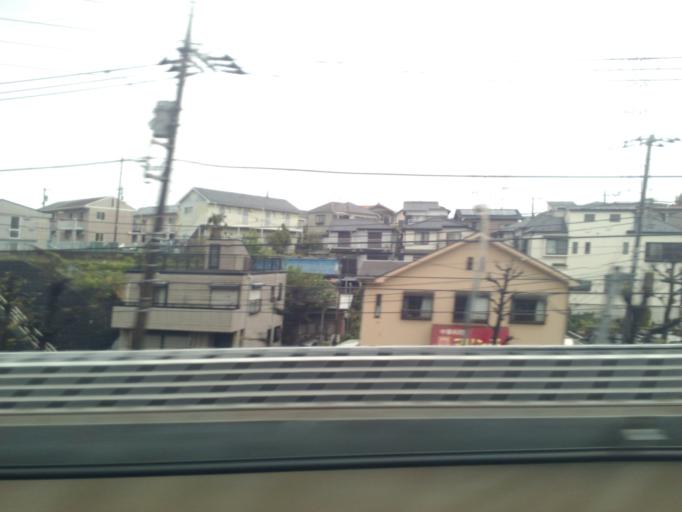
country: JP
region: Kanagawa
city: Minami-rinkan
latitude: 35.4478
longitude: 139.5066
